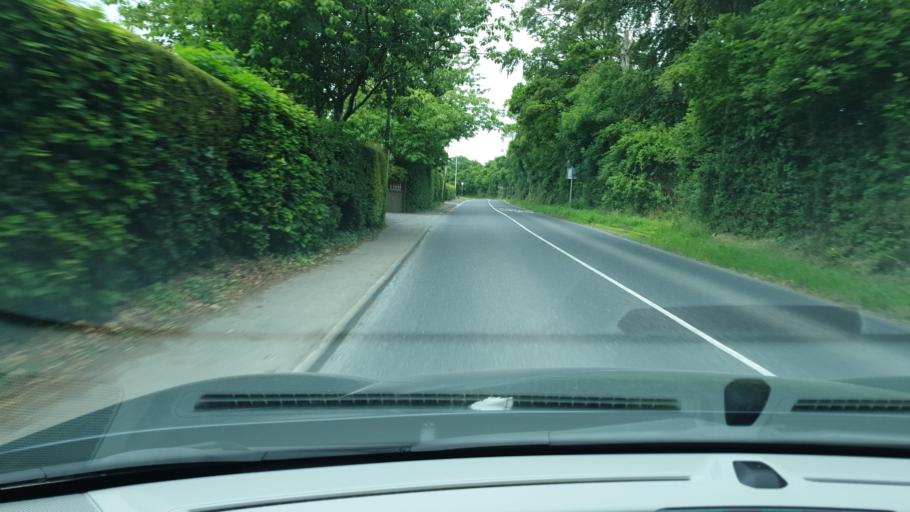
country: IE
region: Leinster
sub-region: An Mhi
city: Dunshaughlin
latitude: 53.4678
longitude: -6.5347
